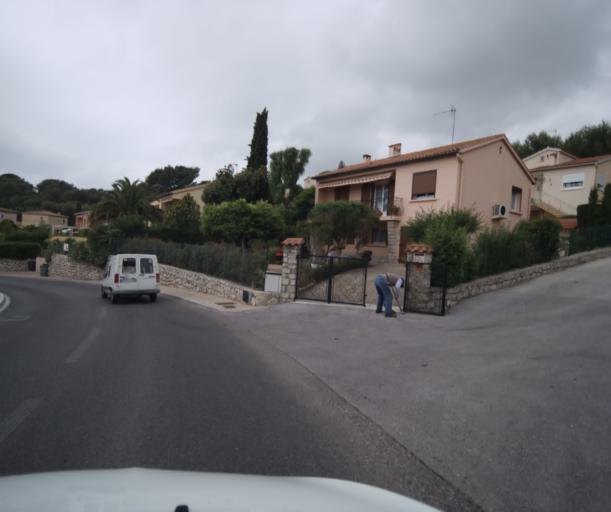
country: FR
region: Provence-Alpes-Cote d'Azur
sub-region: Departement du Var
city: La Garde
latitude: 43.1258
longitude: 5.9979
